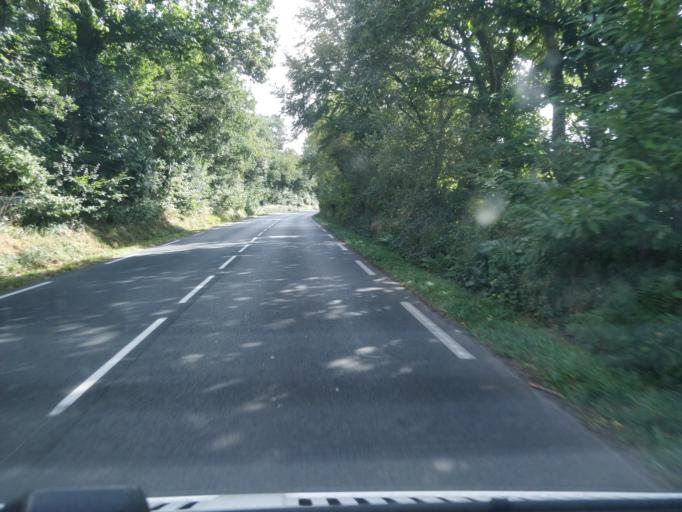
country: FR
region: Brittany
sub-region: Departement du Finistere
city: Plogastel-Saint-Germain
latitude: 47.9998
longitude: -4.2979
